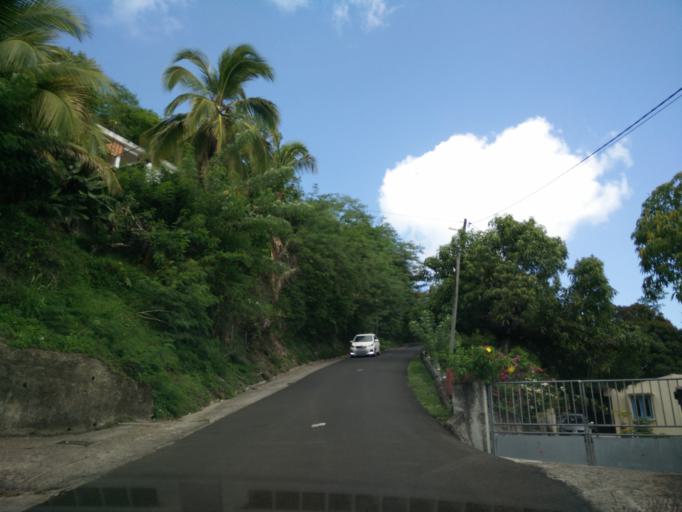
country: MQ
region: Martinique
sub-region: Martinique
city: Les Trois-Ilets
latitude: 14.4839
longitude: -61.0786
